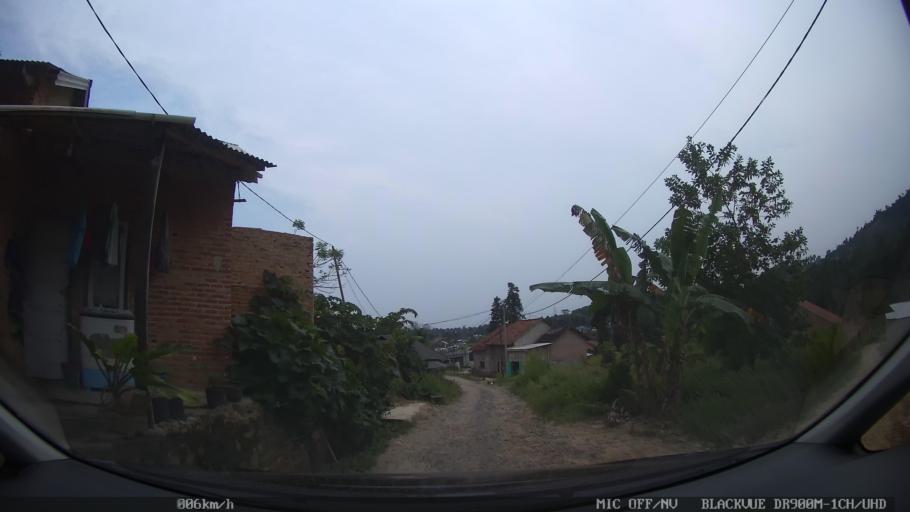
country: ID
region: Lampung
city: Panjang
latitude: -5.4275
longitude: 105.3397
